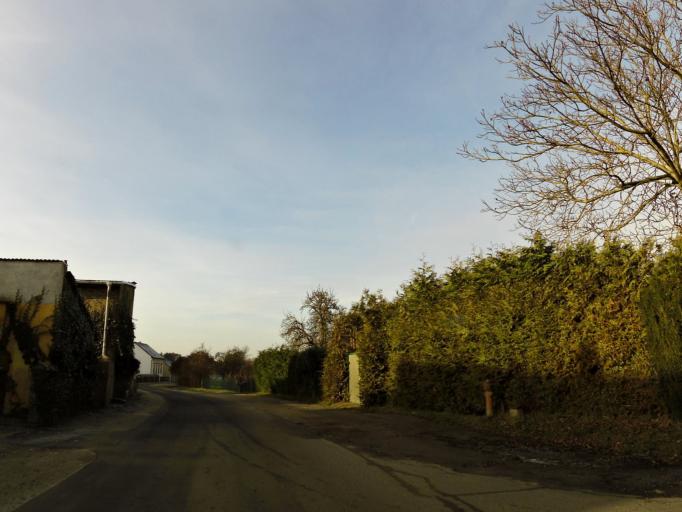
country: DE
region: Brandenburg
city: Werder
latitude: 52.3565
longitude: 12.9157
